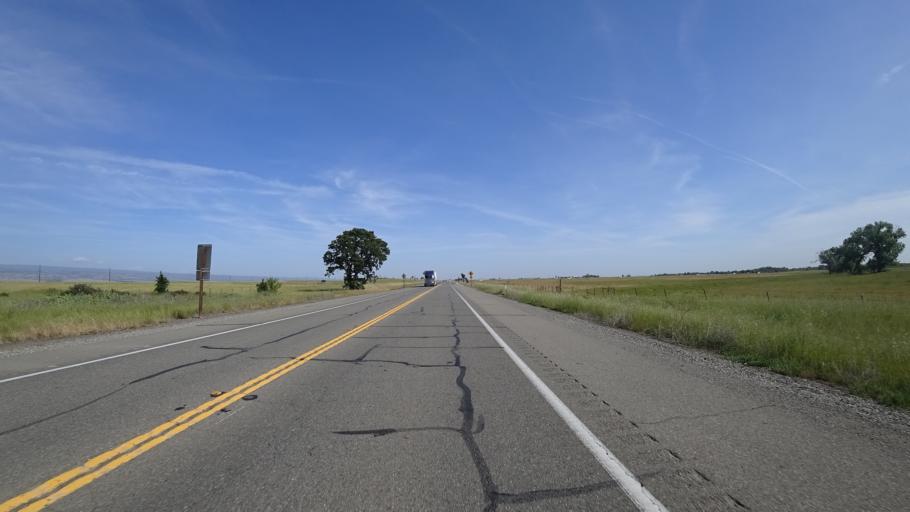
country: US
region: California
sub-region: Tehama County
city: Los Molinos
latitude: 39.9353
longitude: -122.0371
